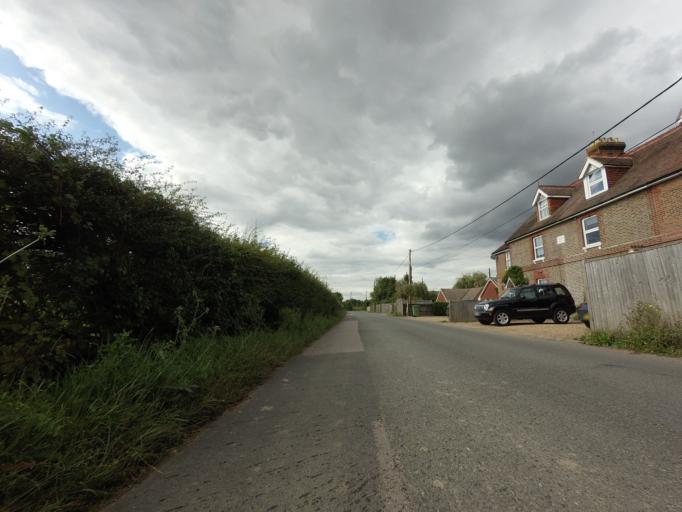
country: GB
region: England
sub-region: Kent
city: Paddock Wood
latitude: 51.1670
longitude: 0.4221
